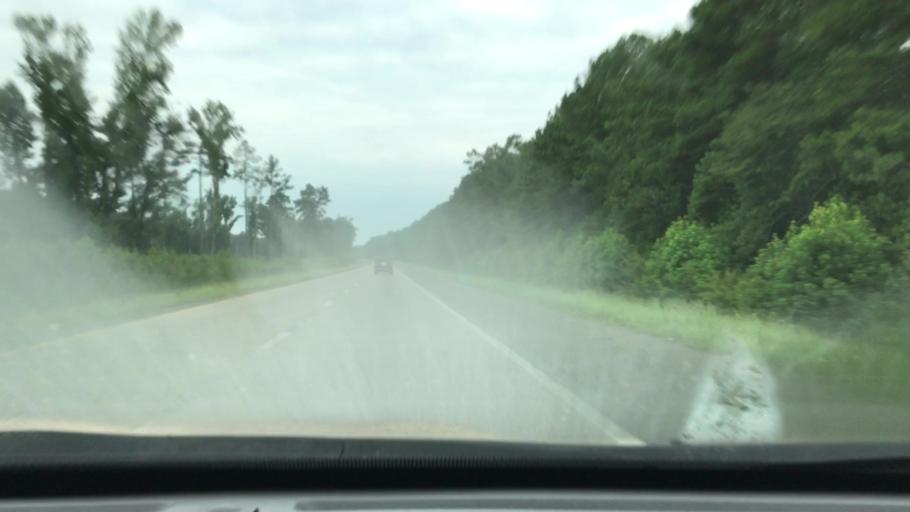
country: US
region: South Carolina
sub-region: Colleton County
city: Walterboro
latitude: 32.8631
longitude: -80.7266
